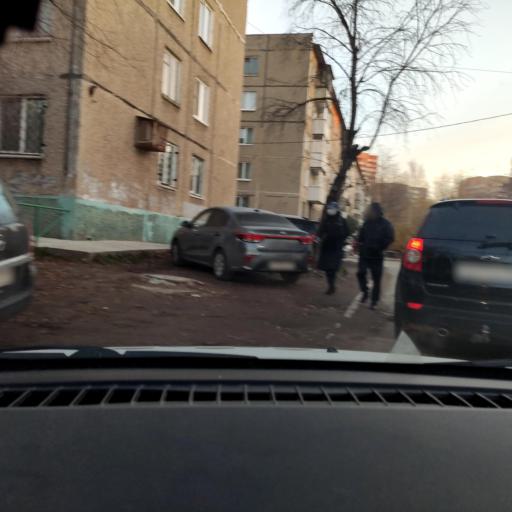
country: RU
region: Perm
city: Perm
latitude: 58.0600
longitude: 56.3543
